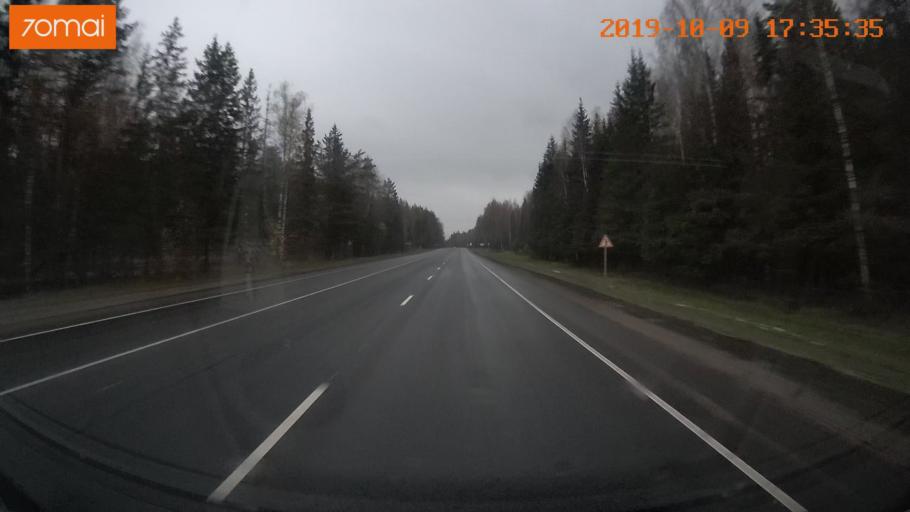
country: RU
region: Ivanovo
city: Bogorodskoye
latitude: 57.0912
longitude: 41.0011
